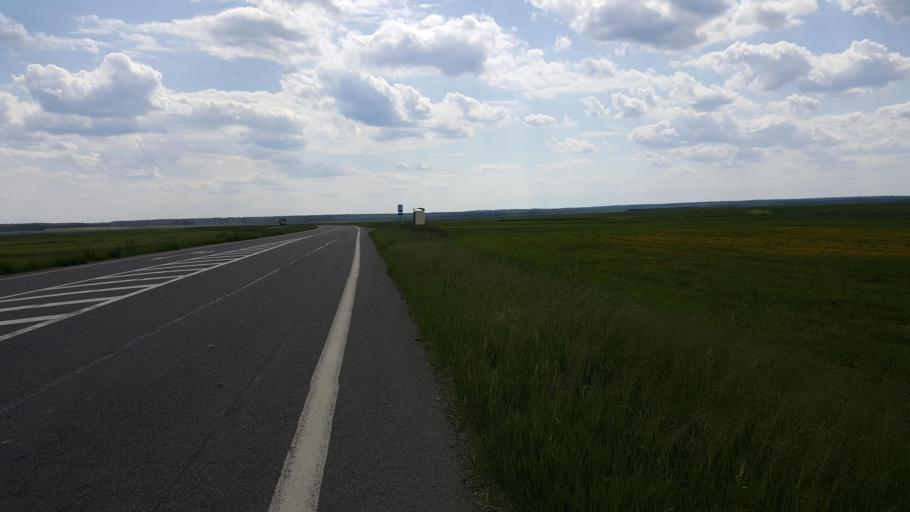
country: PL
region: Podlasie
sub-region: Powiat hajnowski
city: Bialowieza
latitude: 52.6550
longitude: 24.0869
